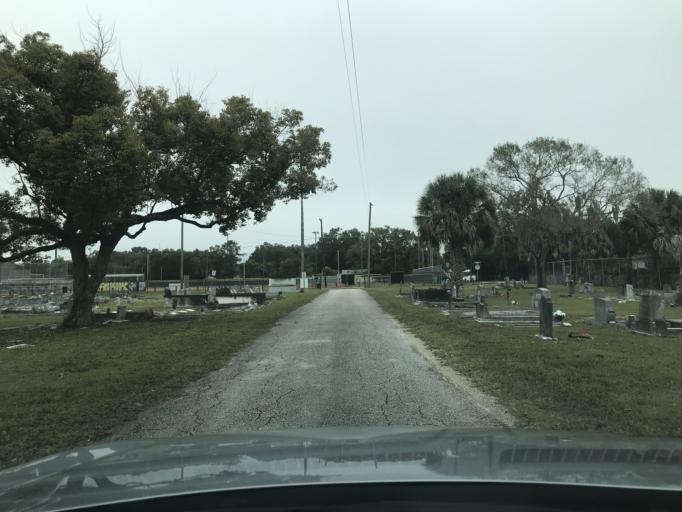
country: US
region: Florida
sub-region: Hillsborough County
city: Tampa
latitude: 27.9772
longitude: -82.4648
